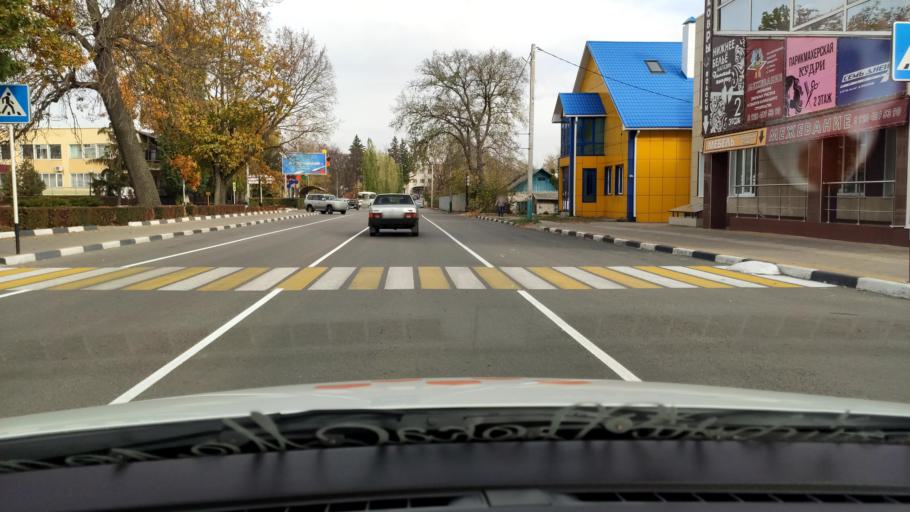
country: RU
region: Voronezj
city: Ramon'
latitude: 51.9124
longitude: 39.3388
